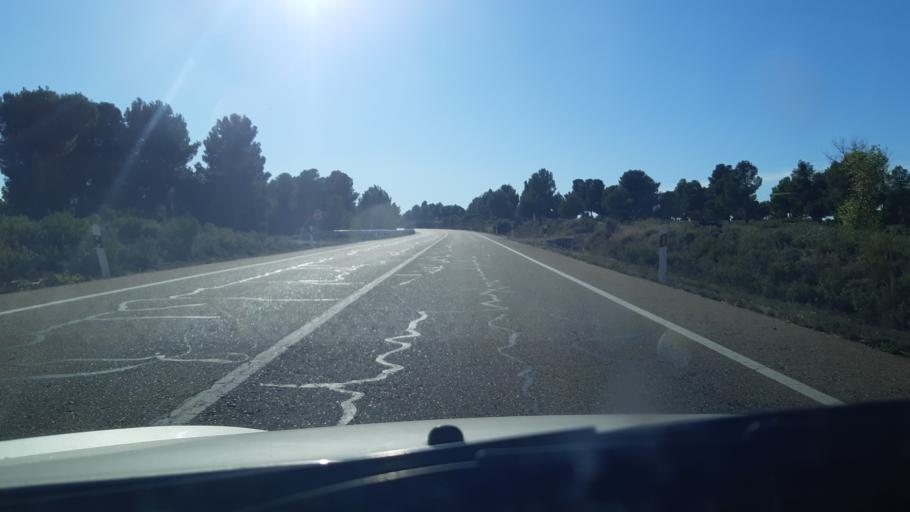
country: ES
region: Aragon
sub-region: Provincia de Teruel
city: Fornoles
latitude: 40.9270
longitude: -0.0155
